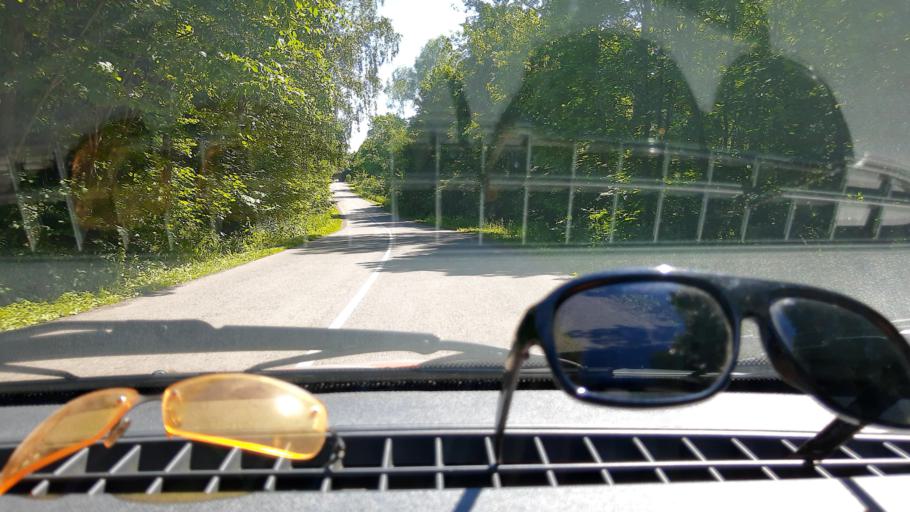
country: RU
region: Bashkortostan
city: Ulu-Telyak
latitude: 54.8112
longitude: 57.0374
